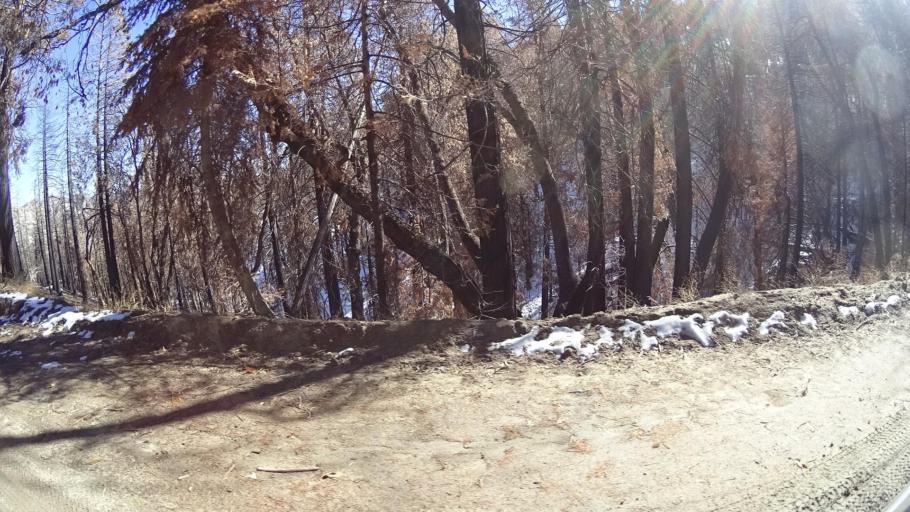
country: US
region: California
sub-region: Kern County
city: Alta Sierra
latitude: 35.7166
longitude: -118.5440
